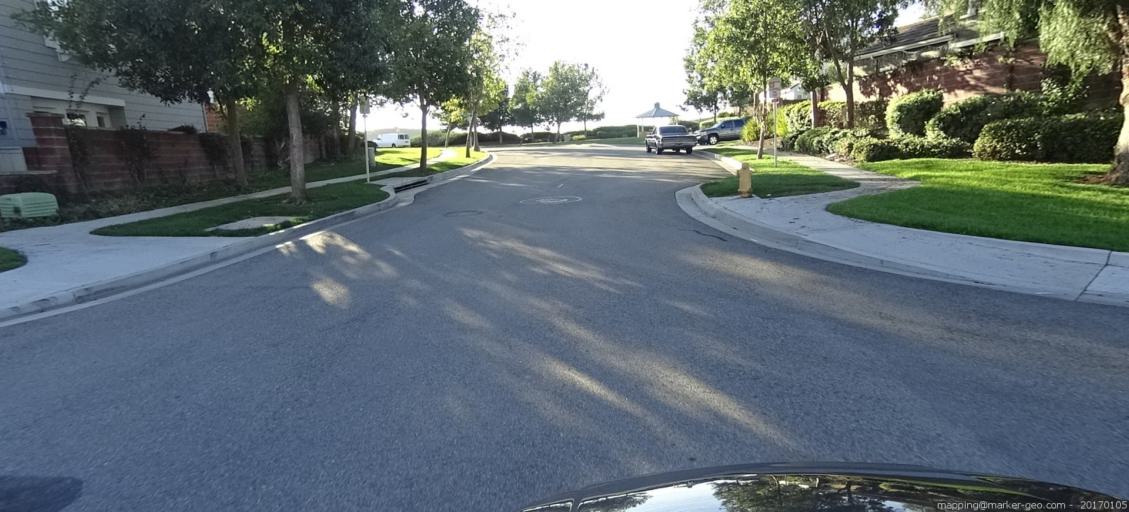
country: US
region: California
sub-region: Orange County
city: Ladera Ranch
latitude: 33.5496
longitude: -117.6407
